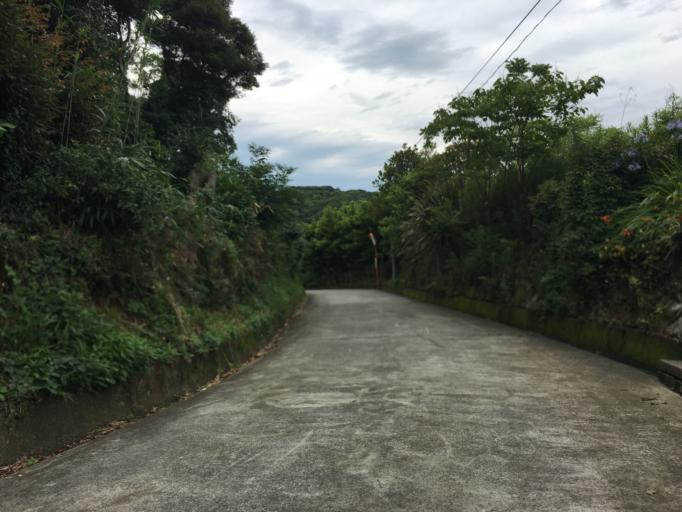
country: JP
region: Aichi
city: Ishiki
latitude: 34.7225
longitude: 137.0490
